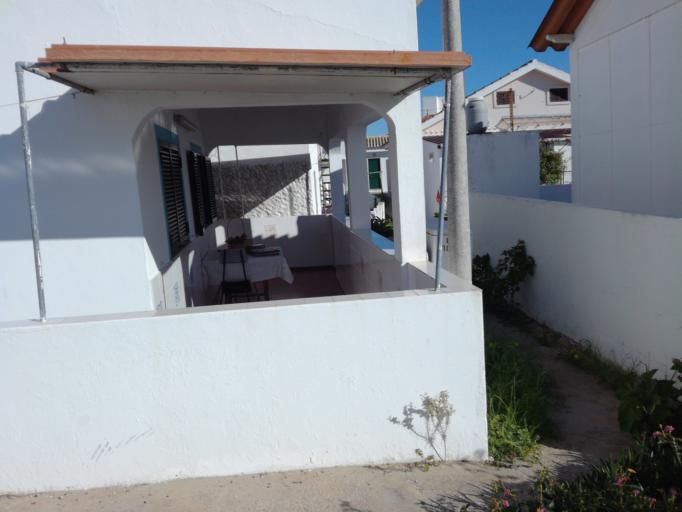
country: PT
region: Faro
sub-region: Olhao
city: Olhao
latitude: 37.0221
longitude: -7.8061
